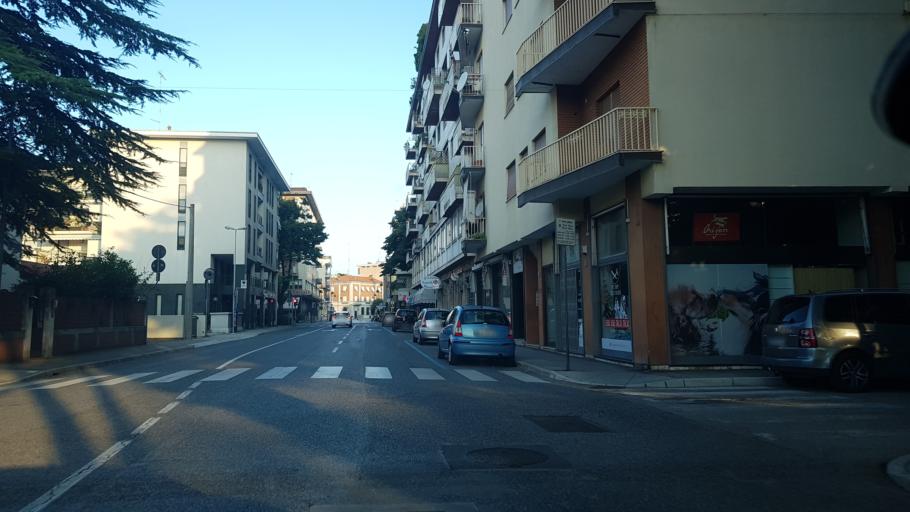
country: IT
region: Friuli Venezia Giulia
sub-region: Provincia di Gorizia
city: Monfalcone
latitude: 45.8072
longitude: 13.5363
